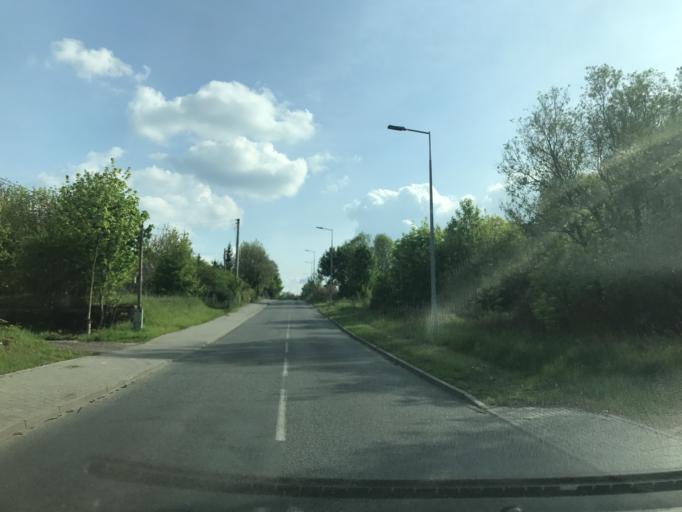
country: PL
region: Kujawsko-Pomorskie
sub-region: Bydgoszcz
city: Fordon
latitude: 53.1134
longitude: 18.1095
